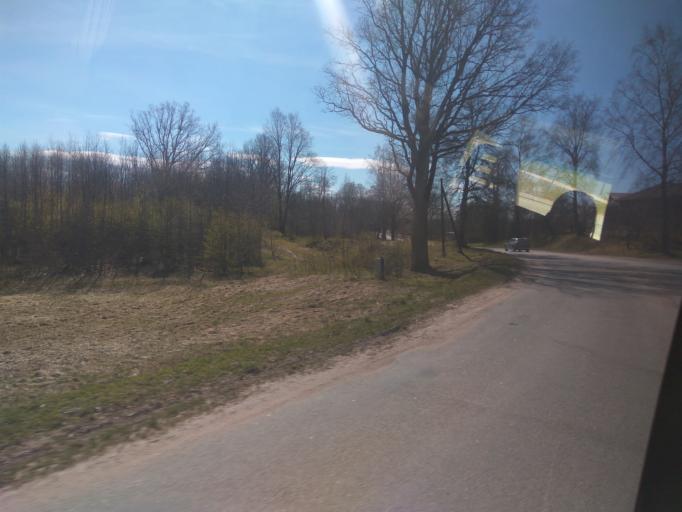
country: LV
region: Aluksnes Rajons
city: Aluksne
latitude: 57.4412
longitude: 27.0371
